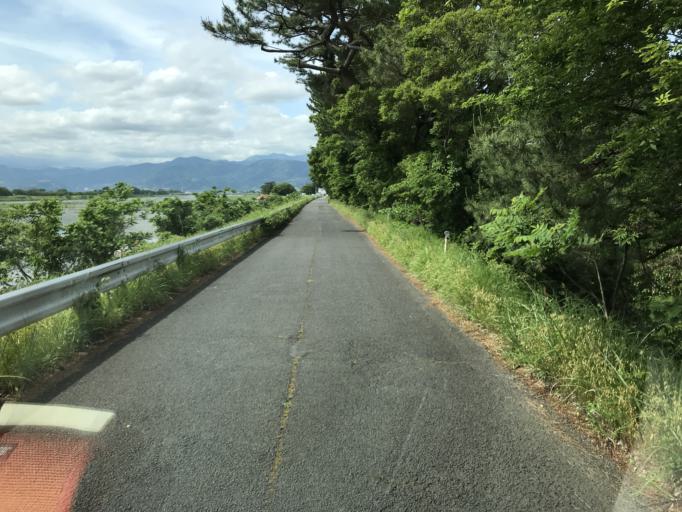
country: JP
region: Kanagawa
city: Odawara
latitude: 35.2975
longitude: 139.1575
